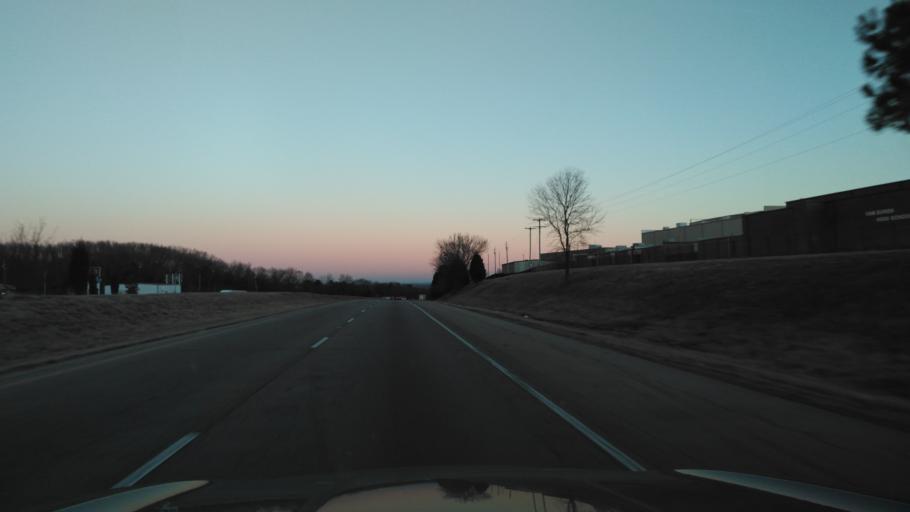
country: US
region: Arkansas
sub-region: Crawford County
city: Van Buren
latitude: 35.4607
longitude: -94.3393
